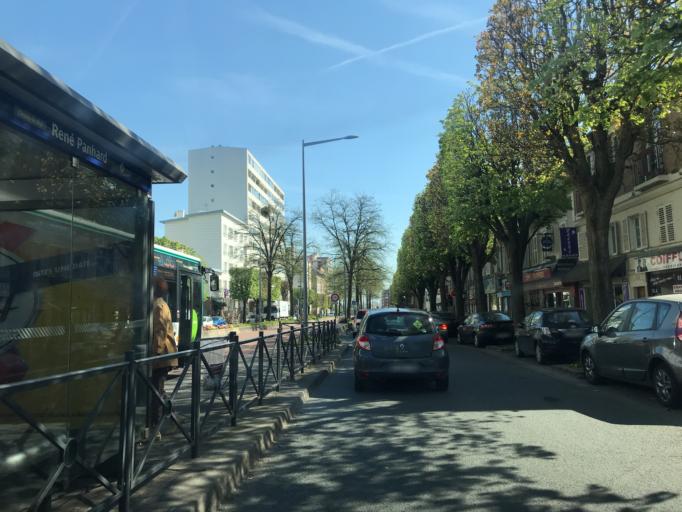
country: FR
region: Ile-de-France
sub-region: Departement du Val-de-Marne
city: Thiais
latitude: 48.7631
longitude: 2.4020
